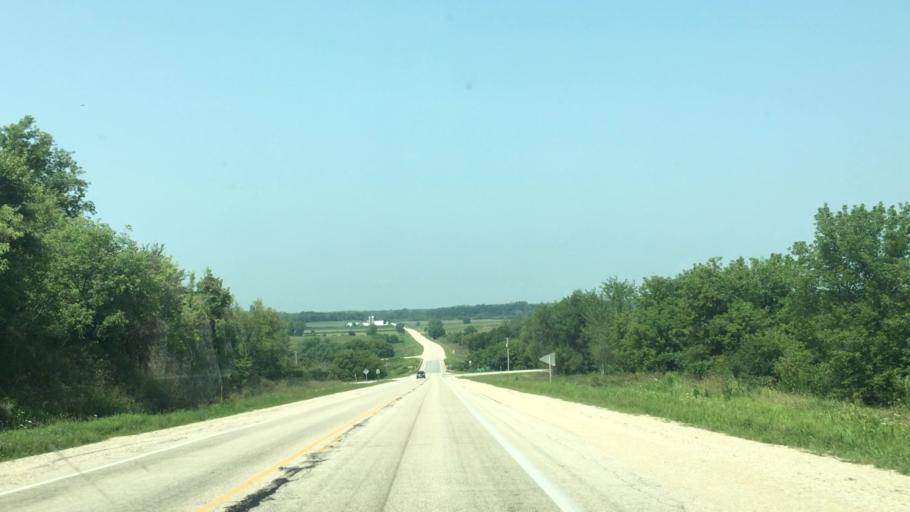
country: US
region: Iowa
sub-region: Fayette County
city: West Union
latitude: 43.0480
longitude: -91.8399
